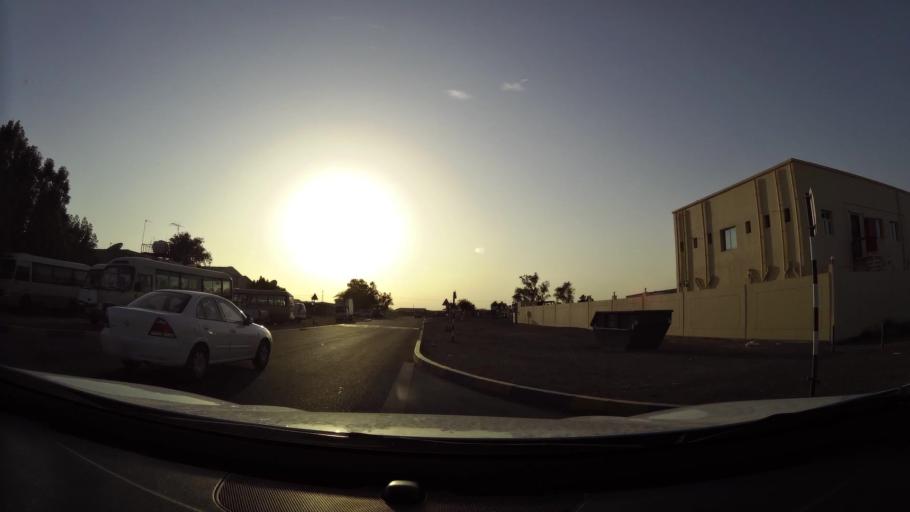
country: AE
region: Abu Dhabi
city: Al Ain
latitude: 24.1554
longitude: 55.8259
